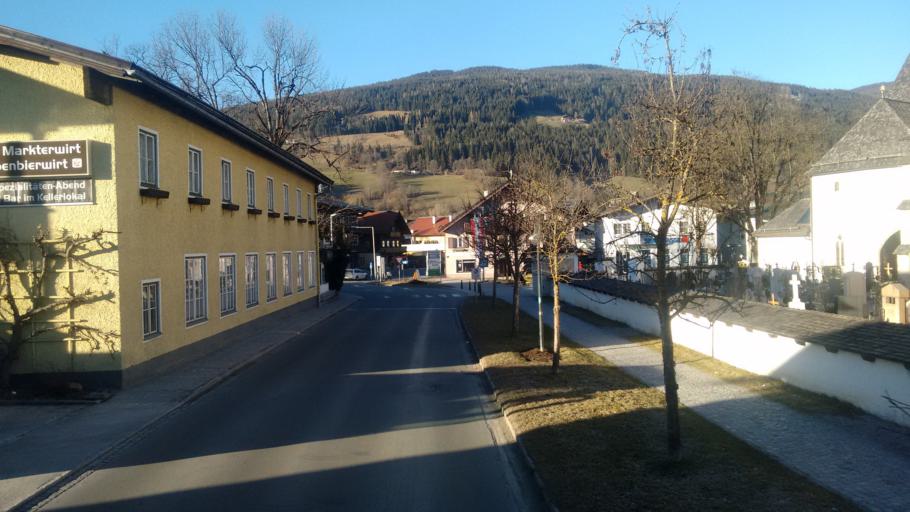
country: AT
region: Salzburg
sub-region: Politischer Bezirk Sankt Johann im Pongau
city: Altenmarkt im Pongau
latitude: 47.3777
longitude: 13.4233
